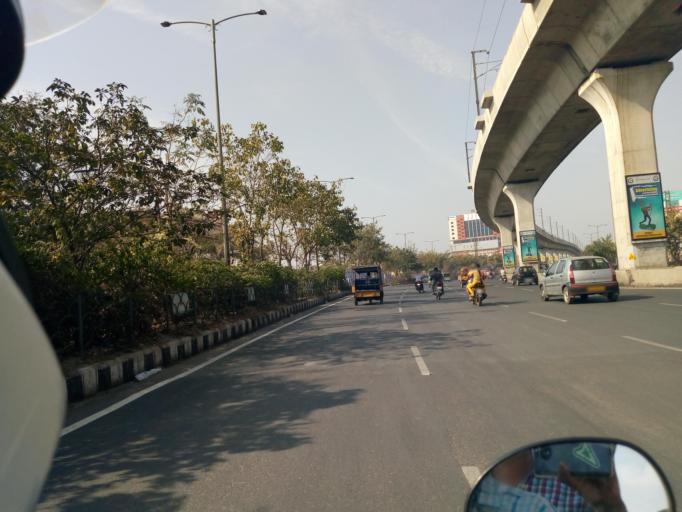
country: IN
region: Telangana
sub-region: Rangareddi
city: Lal Bahadur Nagar
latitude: 17.3513
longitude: 78.5467
